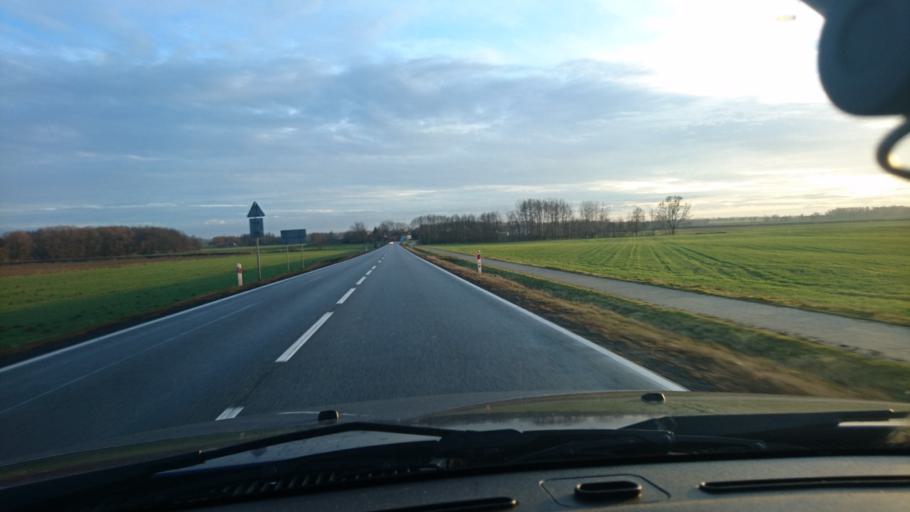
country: PL
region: Greater Poland Voivodeship
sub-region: Powiat kepinski
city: Opatow
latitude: 51.1740
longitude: 18.1450
